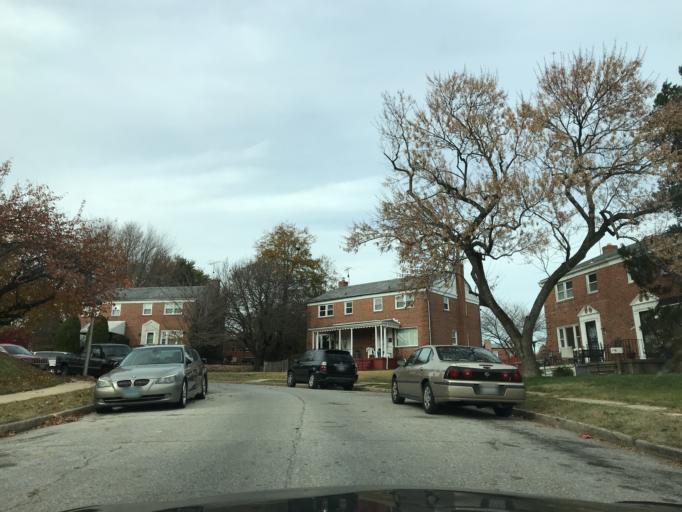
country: US
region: Maryland
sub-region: City of Baltimore
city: Baltimore
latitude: 39.3271
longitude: -76.5744
